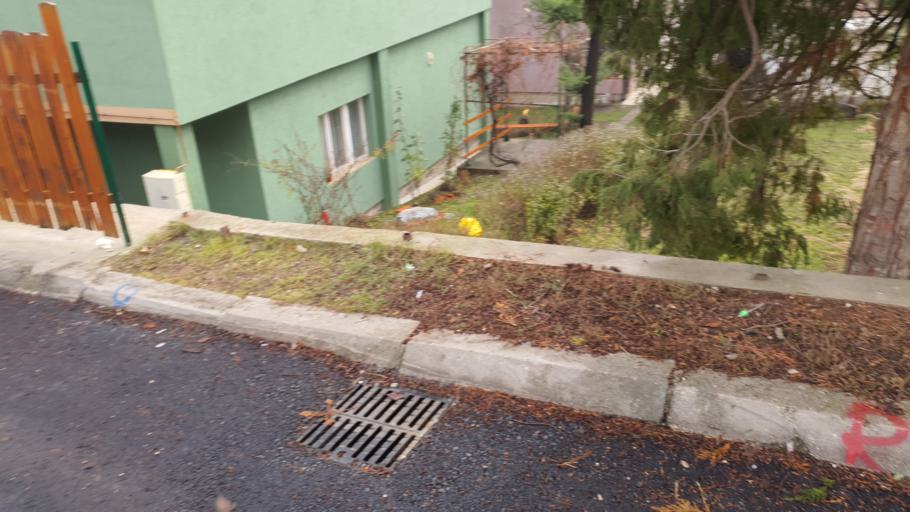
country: RS
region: Central Serbia
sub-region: Zlatiborski Okrug
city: Uzice
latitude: 43.8605
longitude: 19.8206
